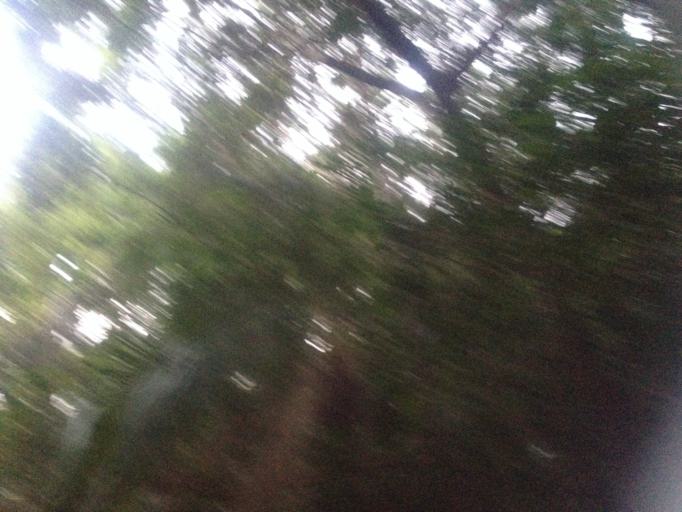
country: BR
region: Sergipe
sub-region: Indiaroba
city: Indiaroba
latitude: -11.4908
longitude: -37.4159
